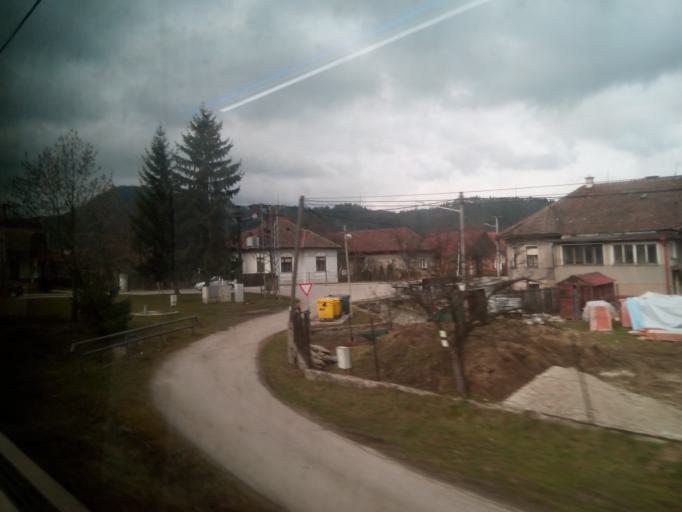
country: SK
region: Zilinsky
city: Ruzomberok
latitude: 49.0878
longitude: 19.3547
